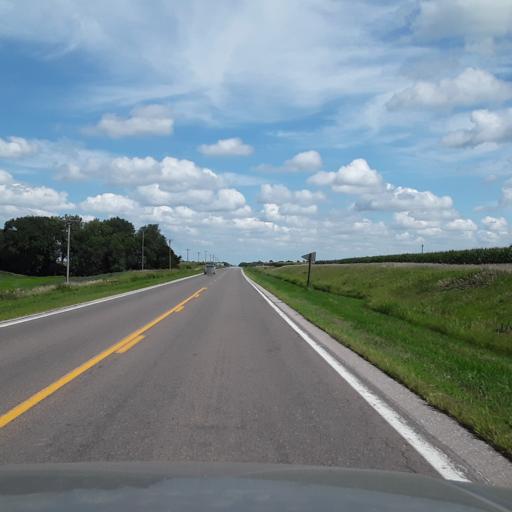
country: US
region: Nebraska
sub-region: Polk County
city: Osceola
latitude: 41.0811
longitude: -97.4254
